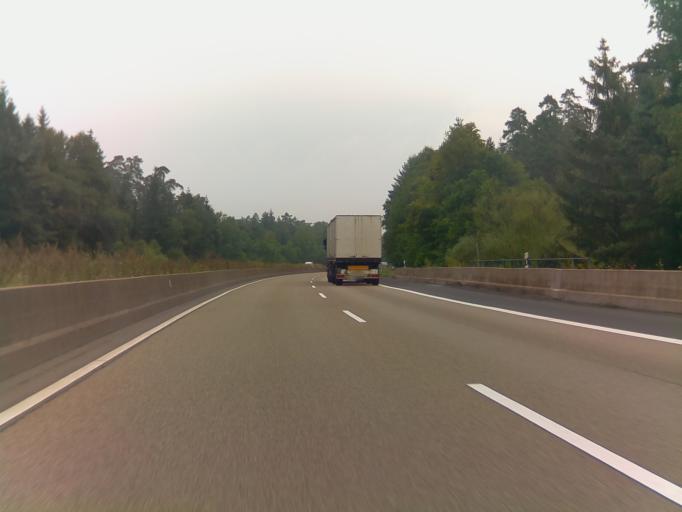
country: DE
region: Hesse
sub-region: Regierungsbezirk Kassel
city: Petersberg
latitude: 50.6288
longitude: 9.6761
